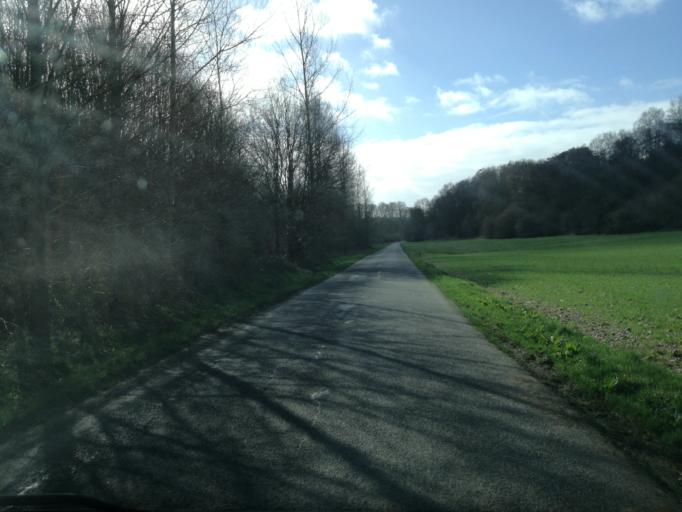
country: FR
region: Haute-Normandie
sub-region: Departement de la Seine-Maritime
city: Yebleron
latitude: 49.6867
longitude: 0.4898
